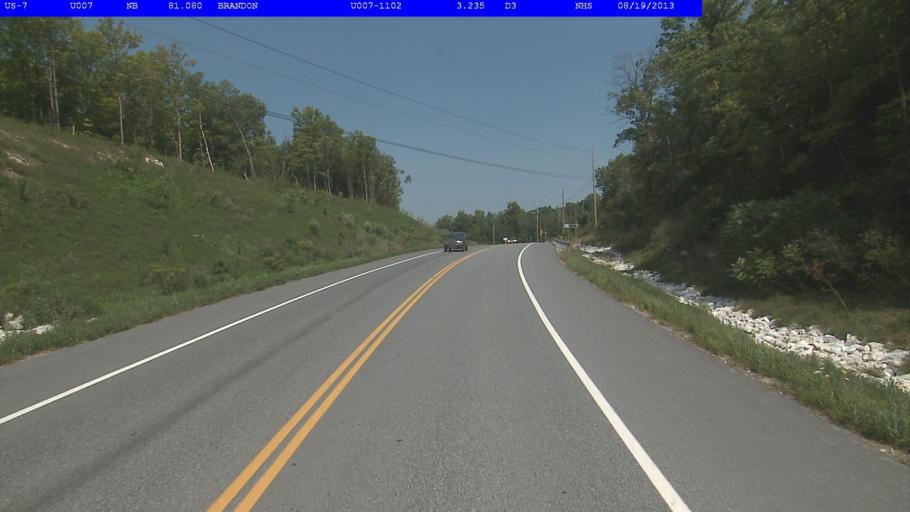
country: US
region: Vermont
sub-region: Rutland County
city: Brandon
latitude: 43.7914
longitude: -73.0785
